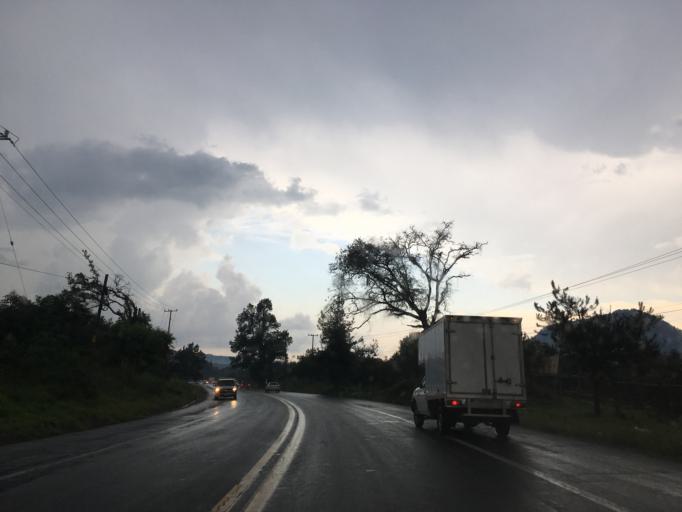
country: MX
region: Michoacan
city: Capacuaro
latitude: 19.4888
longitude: -102.0717
